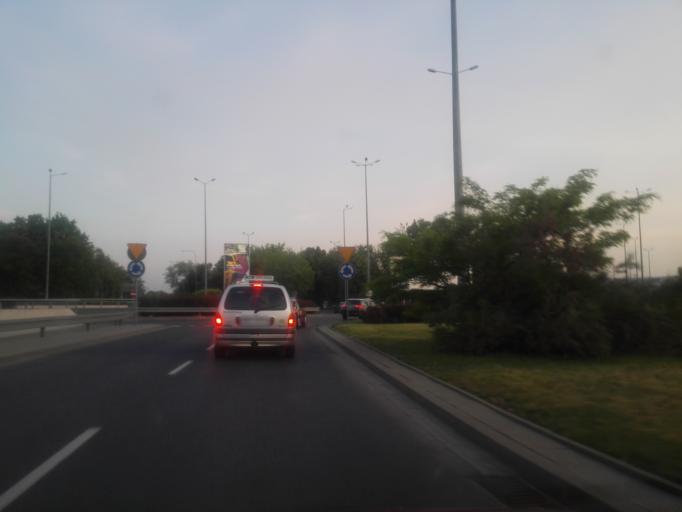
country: PL
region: Masovian Voivodeship
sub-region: Warszawa
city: Wlochy
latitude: 52.1735
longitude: 20.9793
